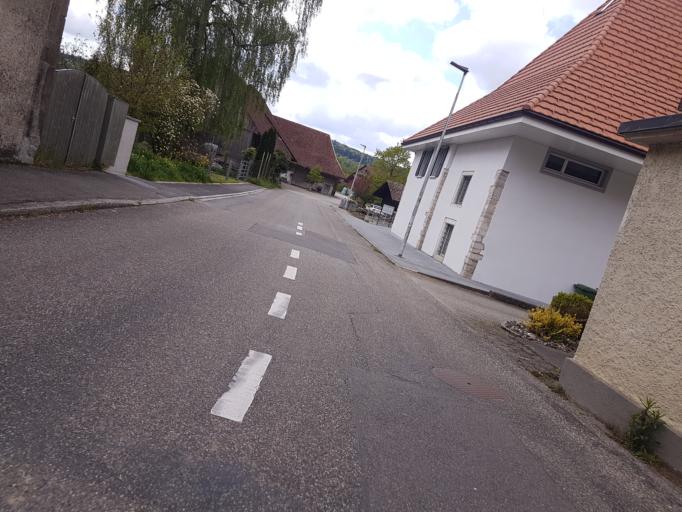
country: CH
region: Solothurn
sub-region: Bezirk Gaeu
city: Wolfwil
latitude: 47.2683
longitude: 7.7976
